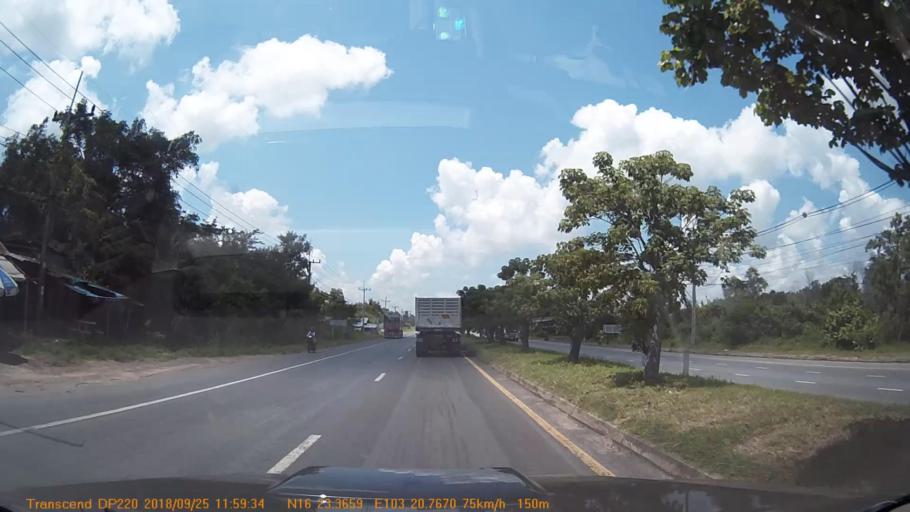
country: TH
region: Kalasin
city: Yang Talat
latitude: 16.3894
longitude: 103.3461
